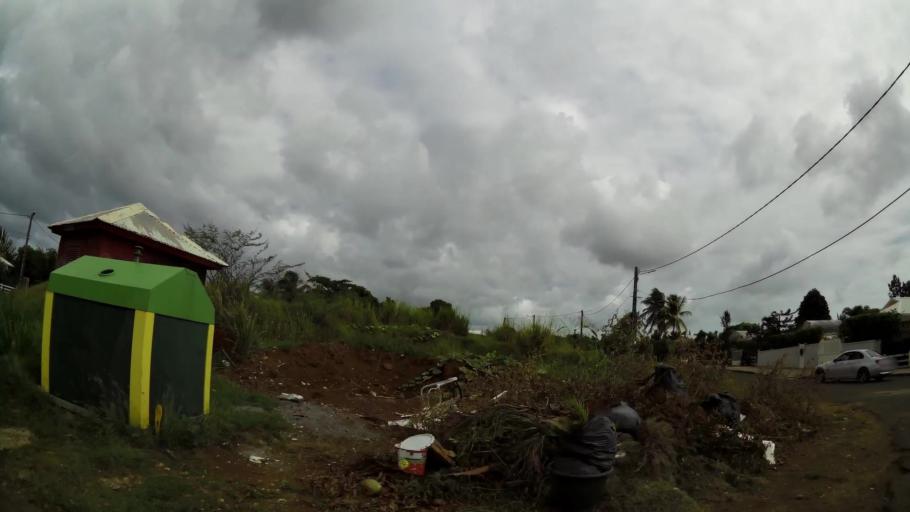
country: GP
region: Guadeloupe
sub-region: Guadeloupe
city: Baie-Mahault
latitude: 16.2565
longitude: -61.5784
